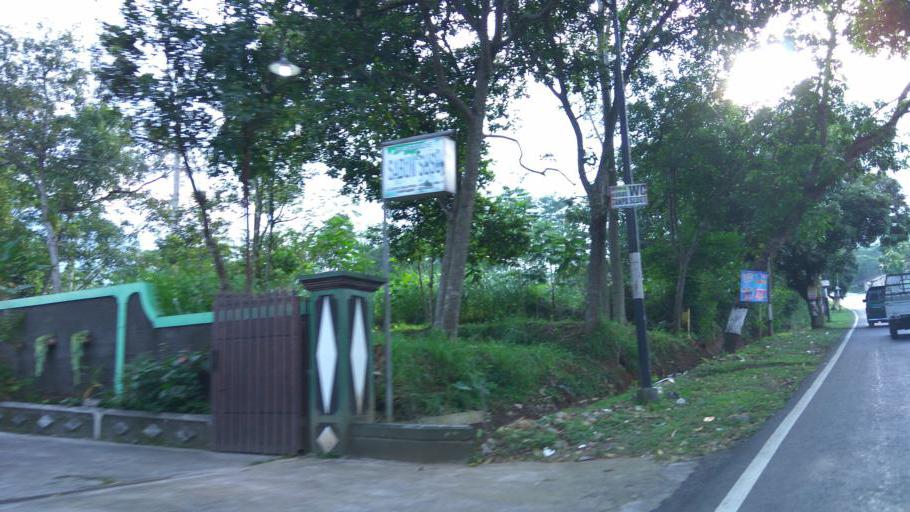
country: ID
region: Central Java
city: Salatiga
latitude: -7.3675
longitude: 110.4599
